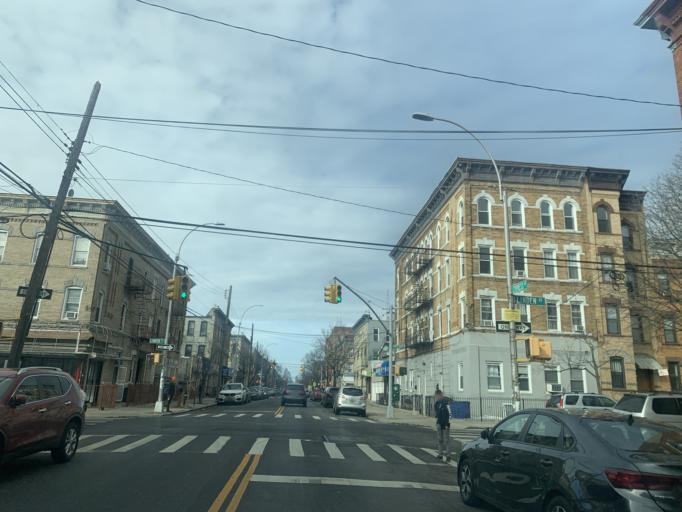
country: US
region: New York
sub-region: Kings County
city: East New York
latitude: 40.7025
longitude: -73.9101
